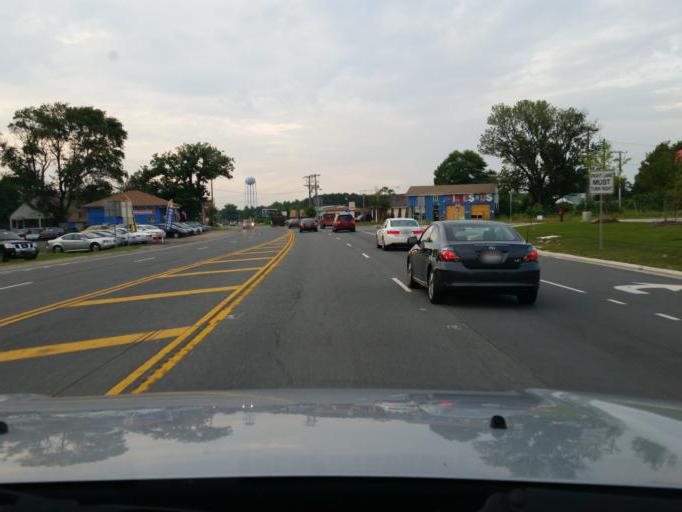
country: US
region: Virginia
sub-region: Spotsylvania County
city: Spotsylvania Courthouse
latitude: 38.1939
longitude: -77.5088
